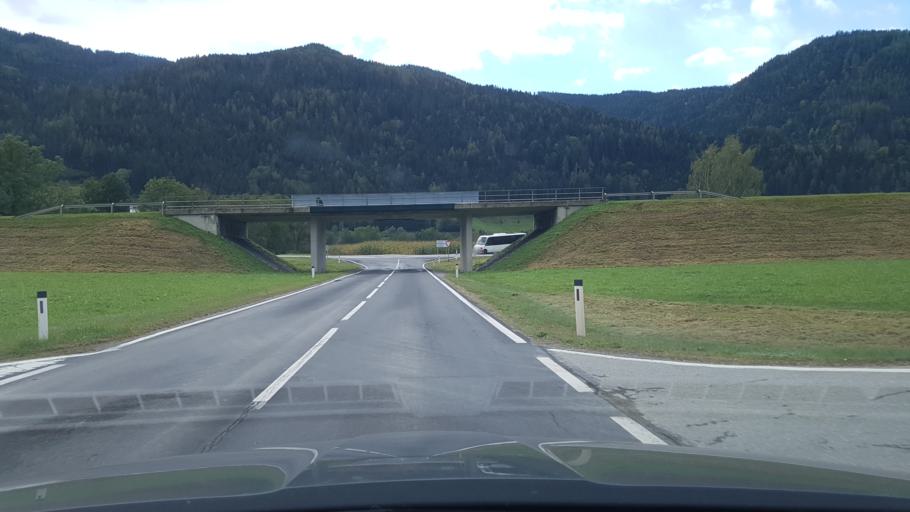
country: AT
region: Styria
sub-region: Politischer Bezirk Murau
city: Sankt Blasen
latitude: 47.1371
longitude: 14.2853
